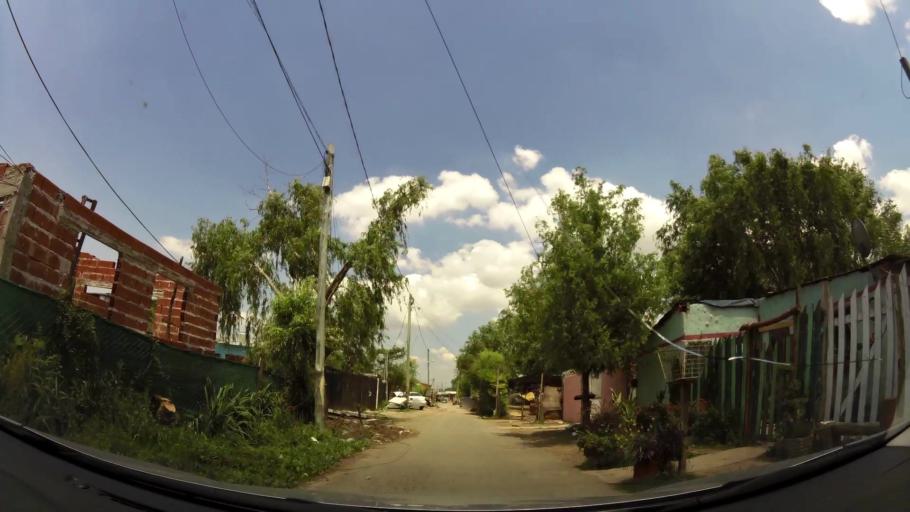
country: AR
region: Buenos Aires
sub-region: Partido de Tigre
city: Tigre
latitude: -34.4069
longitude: -58.6049
